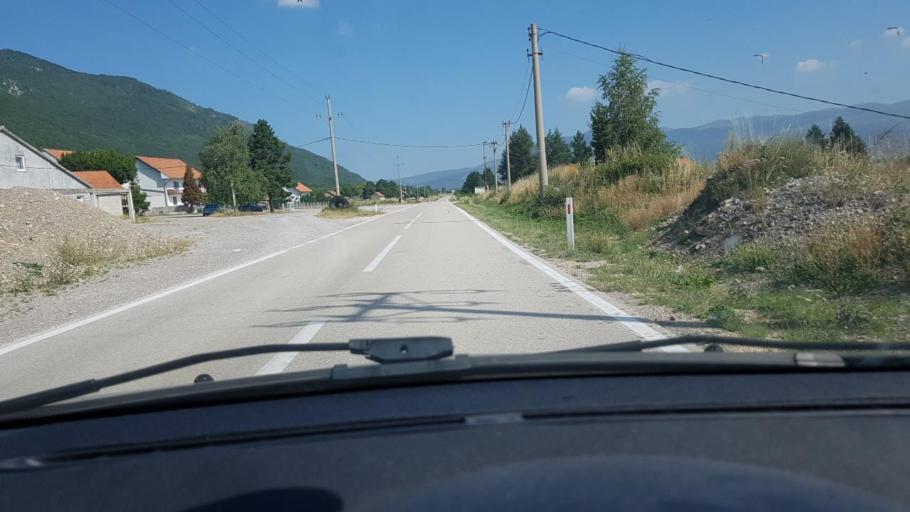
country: BA
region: Federation of Bosnia and Herzegovina
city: Glamoc
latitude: 44.0230
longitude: 16.5989
